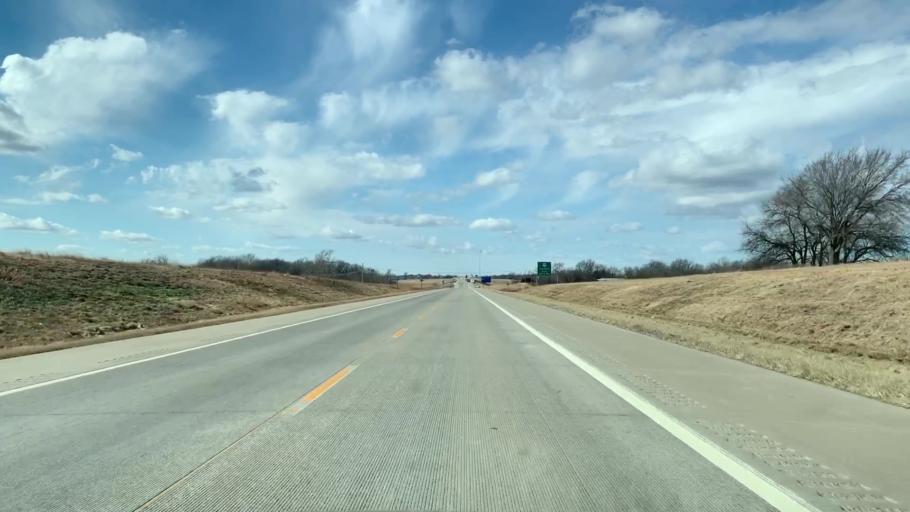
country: US
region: Kansas
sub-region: Labette County
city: Parsons
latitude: 37.3645
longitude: -95.2442
